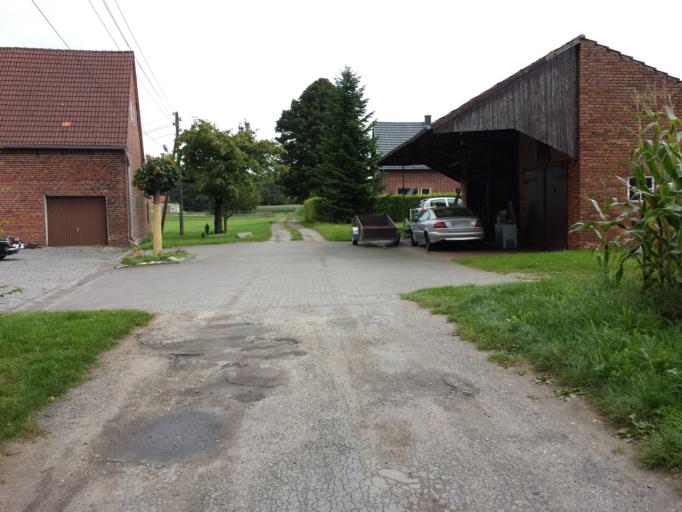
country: DE
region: North Rhine-Westphalia
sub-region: Regierungsbezirk Detmold
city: Guetersloh
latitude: 51.8860
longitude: 8.4013
